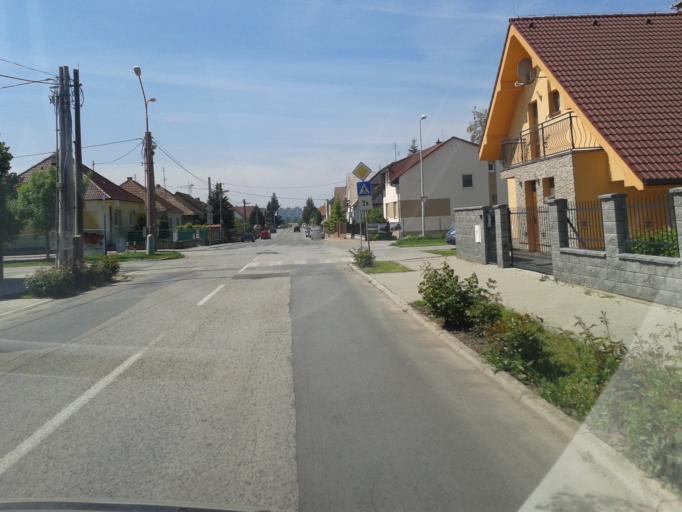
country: SK
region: Trnavsky
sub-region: Okres Trnava
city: Trnava
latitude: 48.3944
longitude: 17.5917
